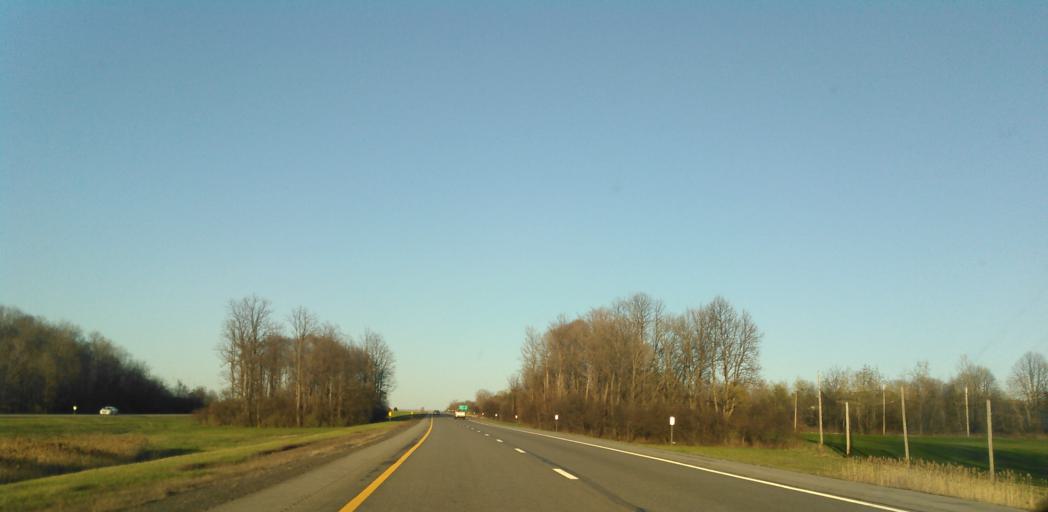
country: US
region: New York
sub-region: Monroe County
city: Honeoye Falls
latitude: 43.0467
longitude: -77.6115
